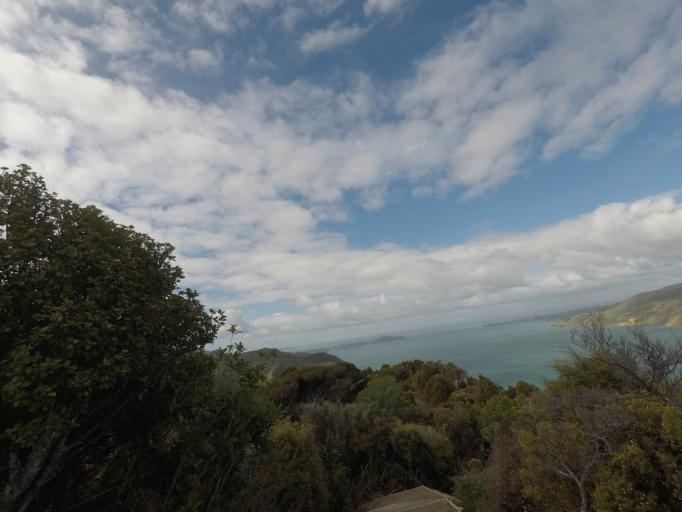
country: NZ
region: Auckland
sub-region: Auckland
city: Titirangi
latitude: -37.0352
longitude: 174.5193
